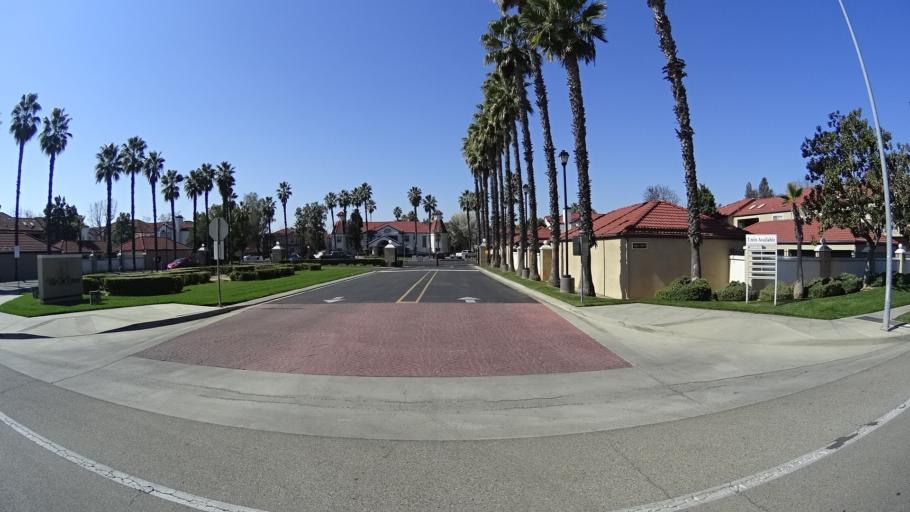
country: US
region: California
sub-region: Fresno County
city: Clovis
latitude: 36.8549
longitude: -119.7568
